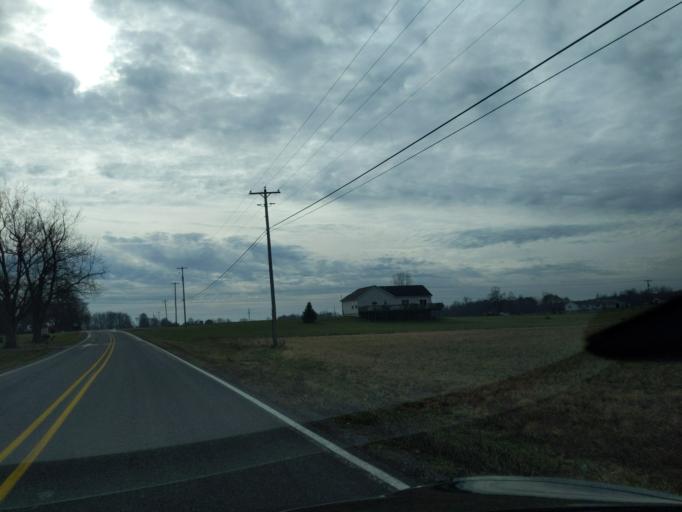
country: US
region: Michigan
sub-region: Ingham County
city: Mason
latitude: 42.5106
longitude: -84.5221
